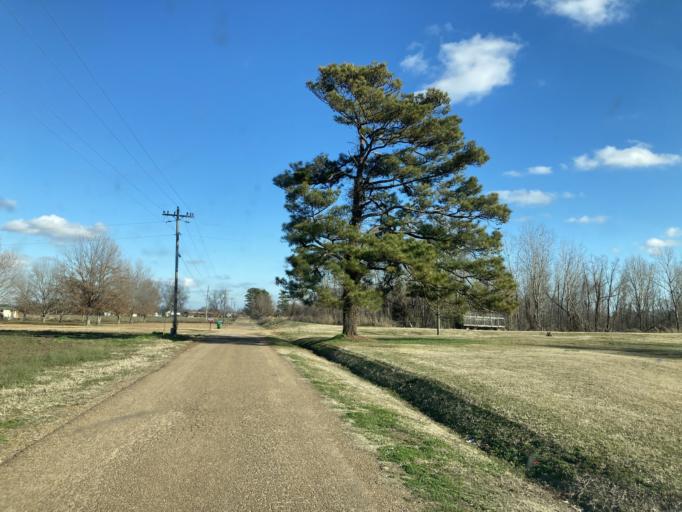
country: US
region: Mississippi
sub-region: Yazoo County
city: Yazoo City
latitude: 32.9350
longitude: -90.4731
